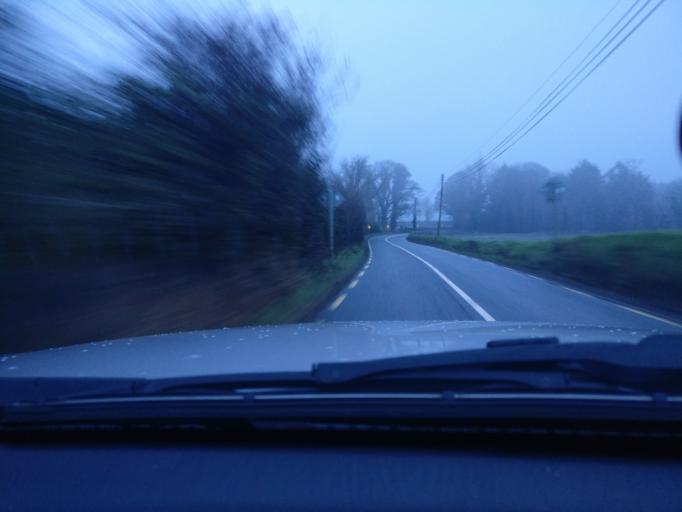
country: IE
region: Leinster
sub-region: An Mhi
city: Athboy
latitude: 53.6141
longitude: -6.9437
